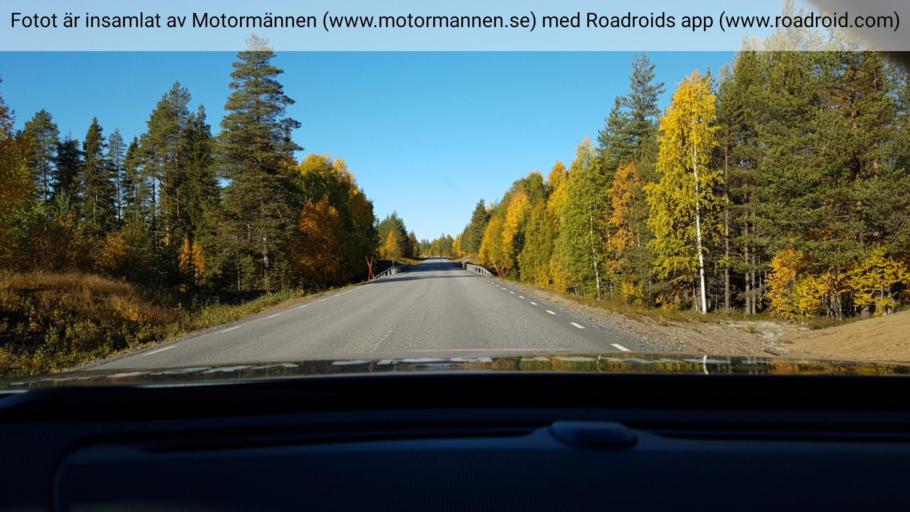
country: SE
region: Vaesterbotten
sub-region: Skelleftea Kommun
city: Storvik
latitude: 65.3357
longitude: 20.8788
